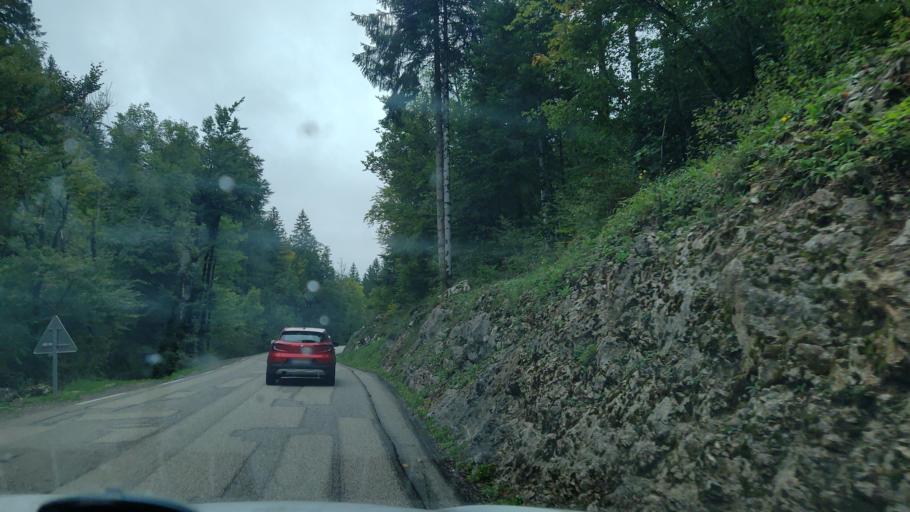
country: FR
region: Rhone-Alpes
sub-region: Departement de l'Isere
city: Saint-Vincent-de-Mercuze
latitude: 45.4371
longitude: 5.8774
